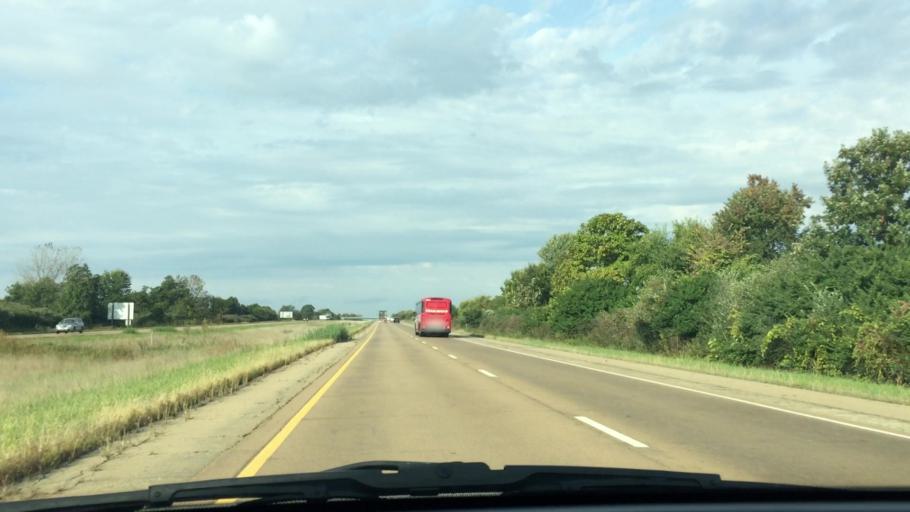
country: US
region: Illinois
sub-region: Whiteside County
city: Rock Falls
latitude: 41.7516
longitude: -89.7186
